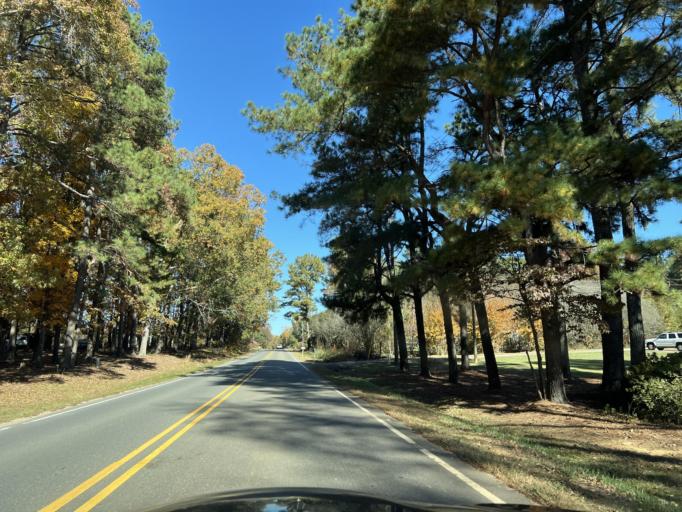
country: US
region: North Carolina
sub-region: Wake County
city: Fuquay-Varina
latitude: 35.6515
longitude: -78.7201
